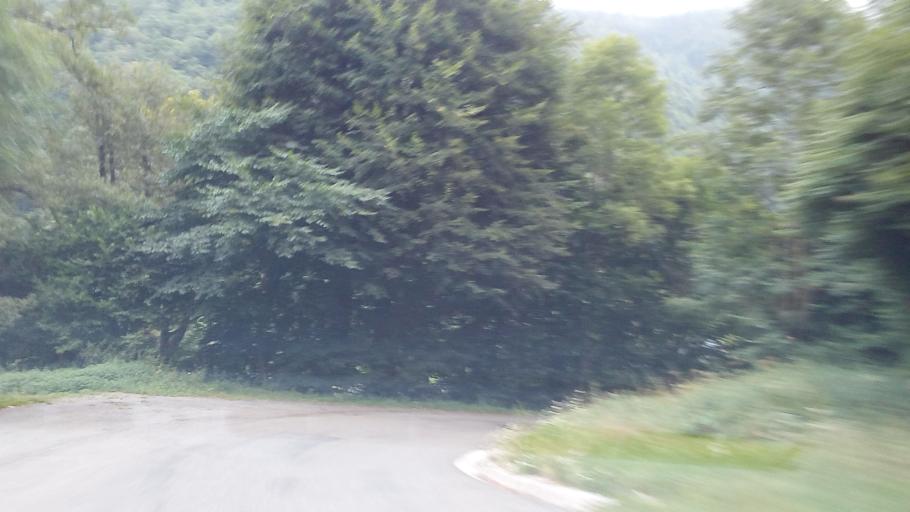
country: FR
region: Midi-Pyrenees
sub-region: Departement des Hautes-Pyrenees
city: Cauterets
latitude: 42.9416
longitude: -0.1790
